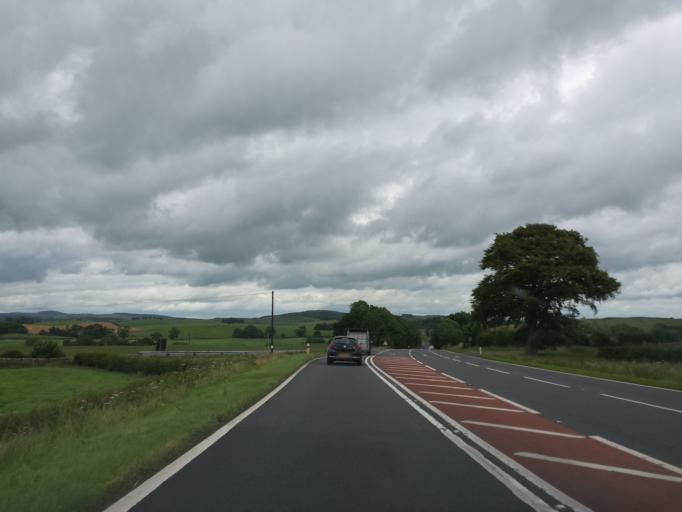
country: GB
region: Scotland
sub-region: Dumfries and Galloway
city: Castle Douglas
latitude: 54.9732
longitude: -3.8966
